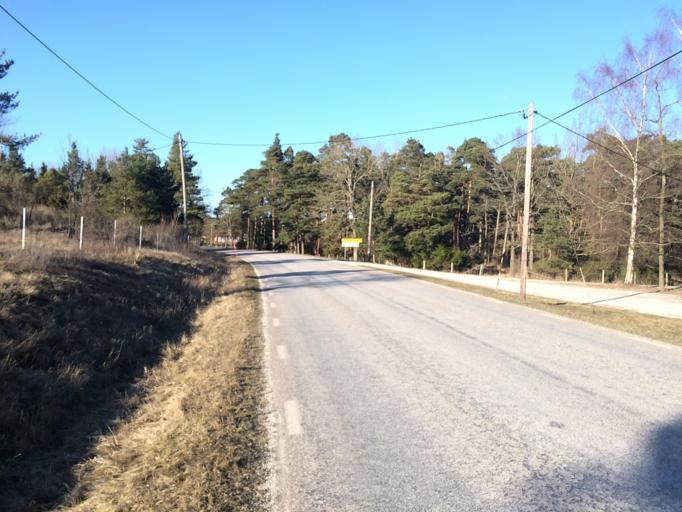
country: SE
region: Gotland
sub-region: Gotland
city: Slite
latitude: 57.5847
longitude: 18.6080
